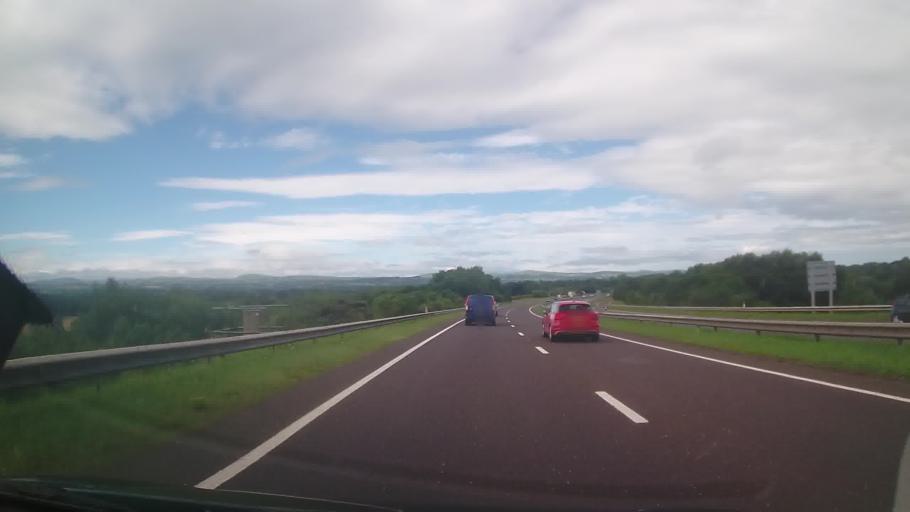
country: GB
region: Wales
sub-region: Denbighshire
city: Cwm
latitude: 53.2602
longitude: -3.3914
